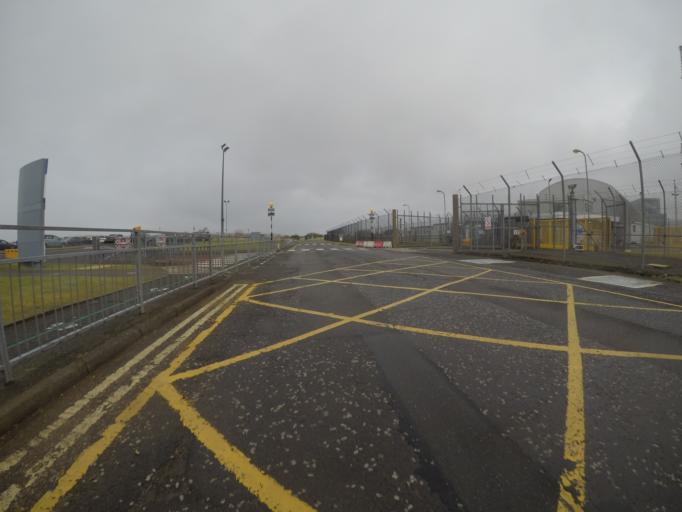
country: GB
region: Scotland
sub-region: North Ayrshire
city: Millport
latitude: 55.7200
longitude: -4.8998
